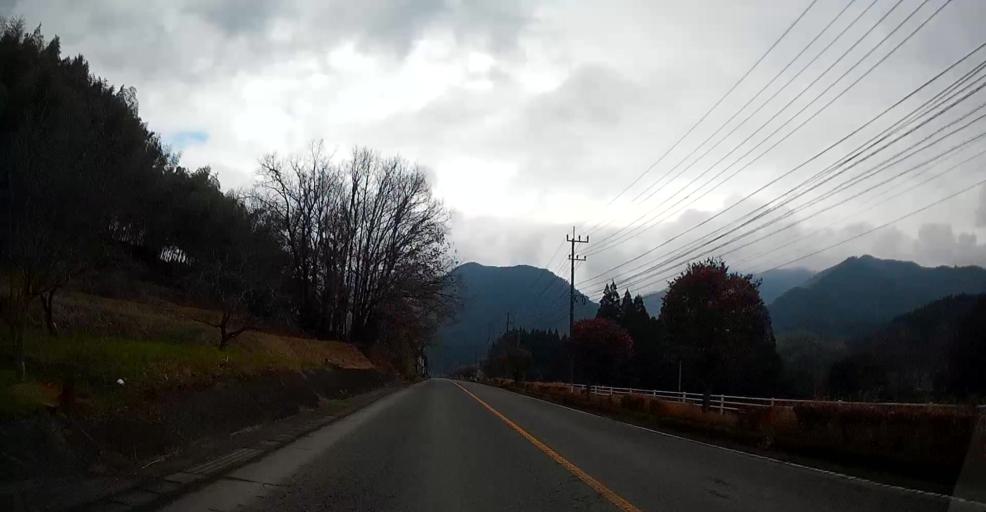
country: JP
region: Kumamoto
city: Matsubase
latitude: 32.6187
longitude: 130.8361
